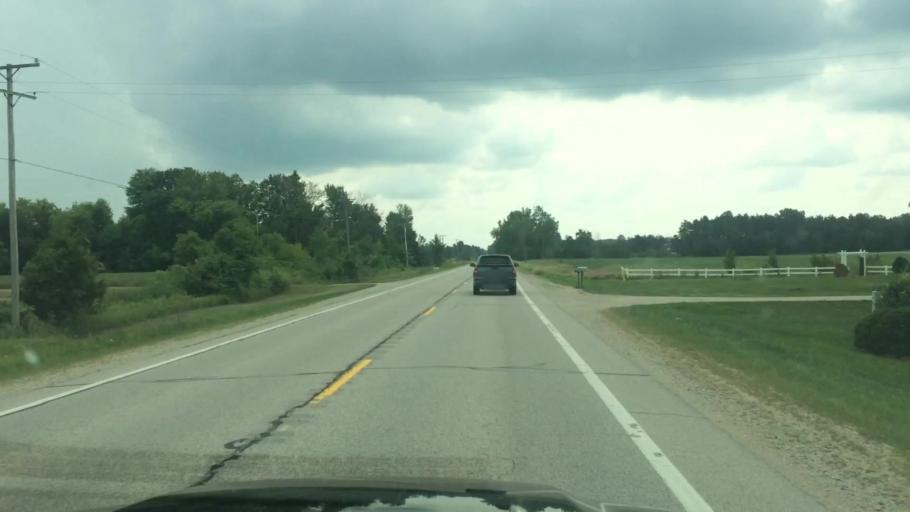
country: US
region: Michigan
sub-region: Tuscola County
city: Cass City
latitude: 43.5122
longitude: -83.0925
